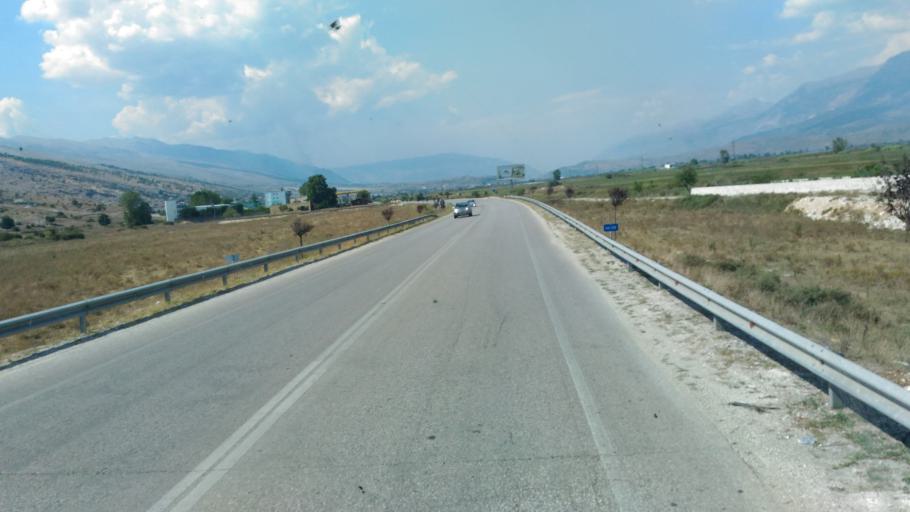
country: AL
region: Gjirokaster
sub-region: Rrethi i Gjirokastres
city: Dervician
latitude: 40.0036
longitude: 20.2106
